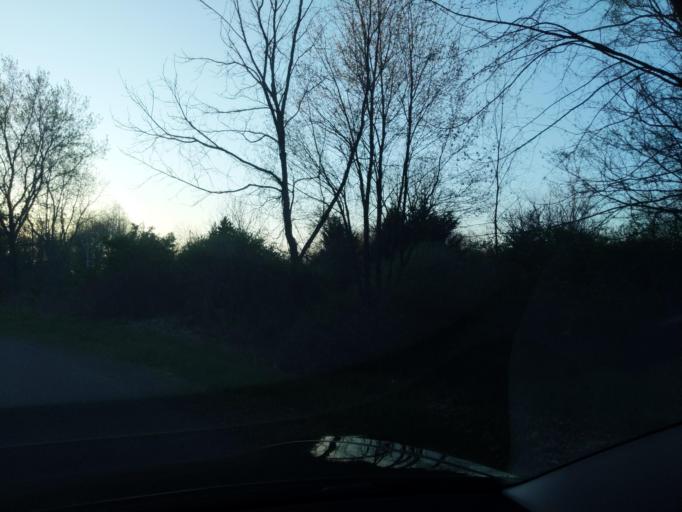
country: US
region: Michigan
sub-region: Ingham County
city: Stockbridge
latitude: 42.4971
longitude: -84.2953
